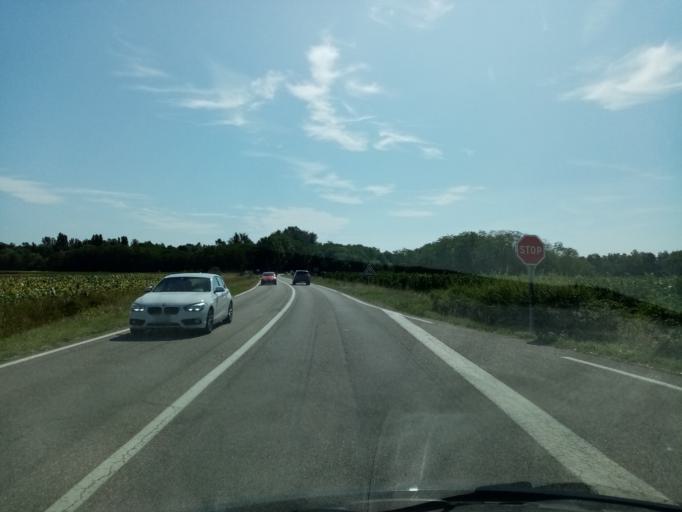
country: FR
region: Alsace
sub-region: Departement du Haut-Rhin
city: Bennwihr
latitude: 48.1340
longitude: 7.3467
